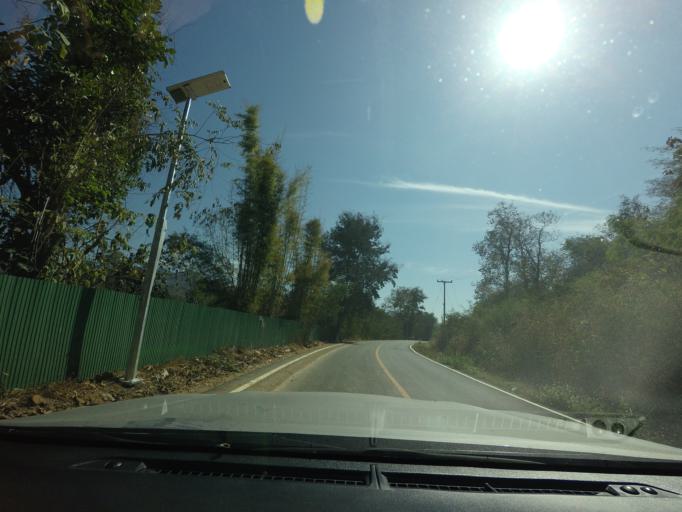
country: TH
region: Mae Hong Son
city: Wiang Nuea
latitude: 19.3772
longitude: 98.4355
